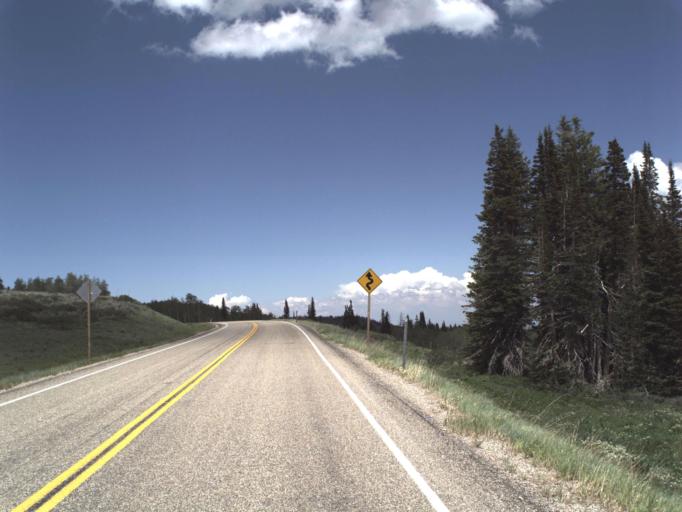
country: US
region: Utah
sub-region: Weber County
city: Wolf Creek
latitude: 41.4413
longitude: -111.5056
